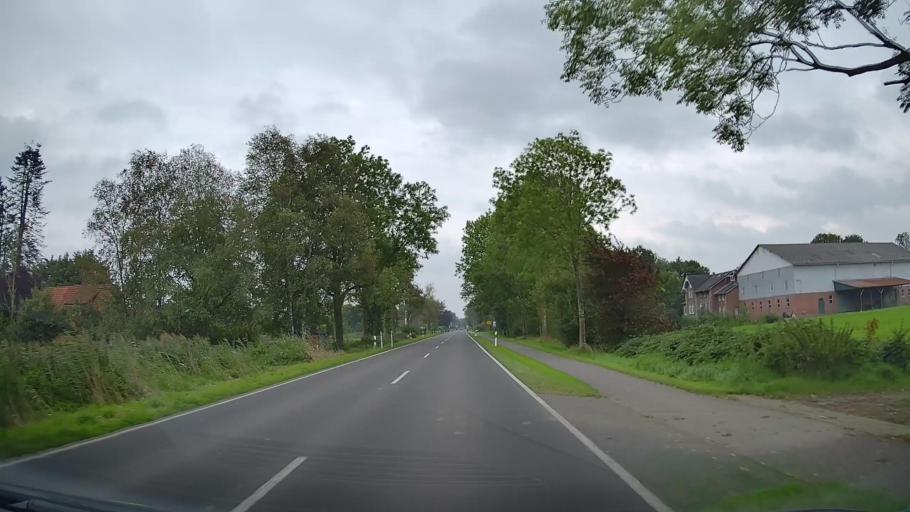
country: DE
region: Lower Saxony
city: Drochtersen
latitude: 53.7240
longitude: 9.3593
